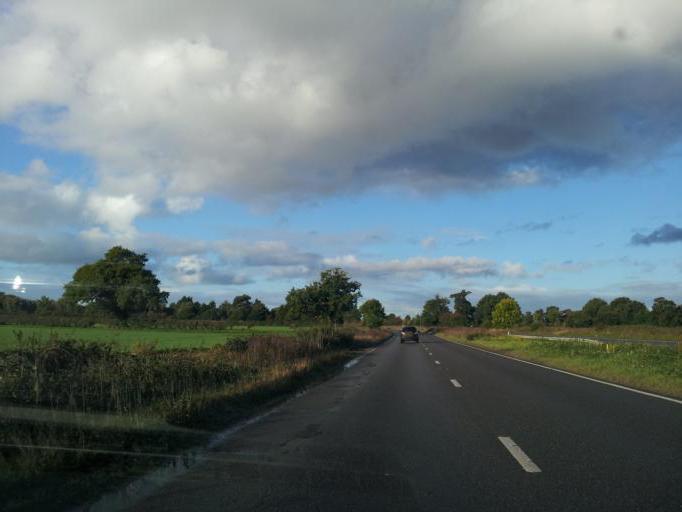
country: GB
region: England
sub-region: Norfolk
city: Brundall
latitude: 52.6312
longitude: 1.4184
